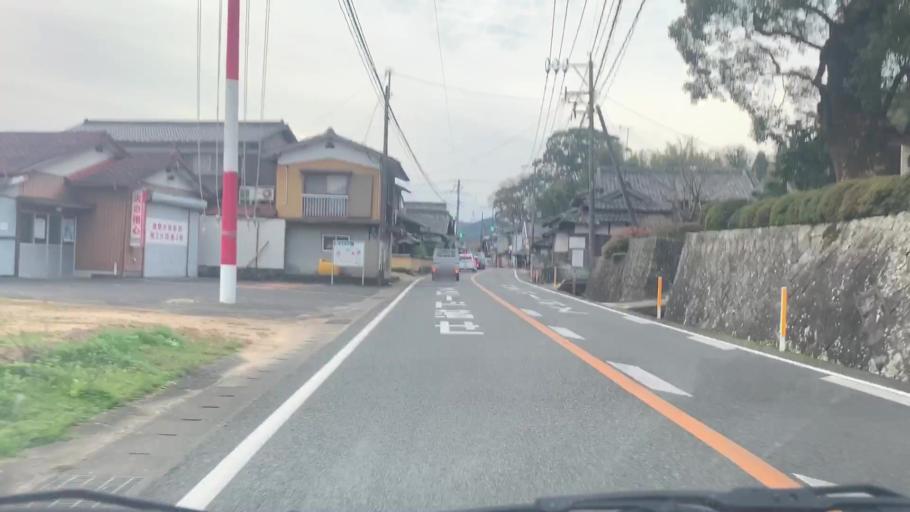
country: JP
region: Saga Prefecture
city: Kashima
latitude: 33.1380
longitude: 130.0639
